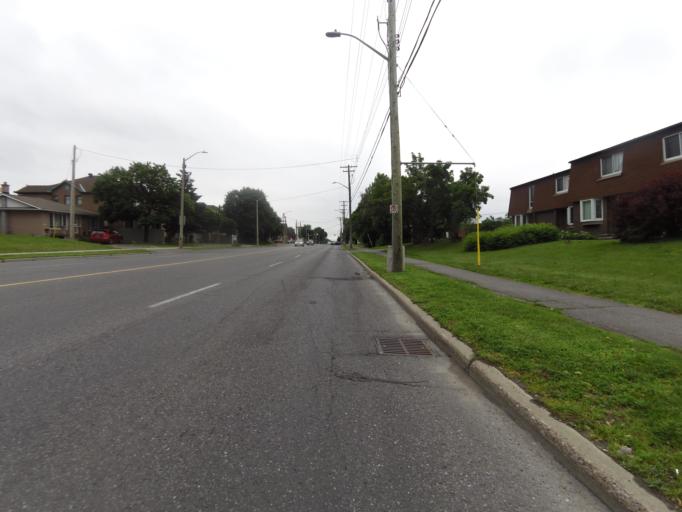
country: CA
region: Ontario
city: Ottawa
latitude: 45.3612
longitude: -75.7107
